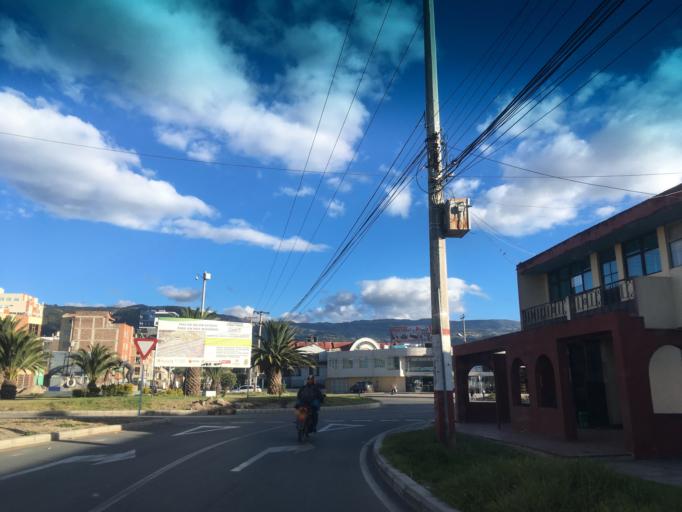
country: CO
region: Boyaca
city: Sogamoso
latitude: 5.7140
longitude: -72.9366
